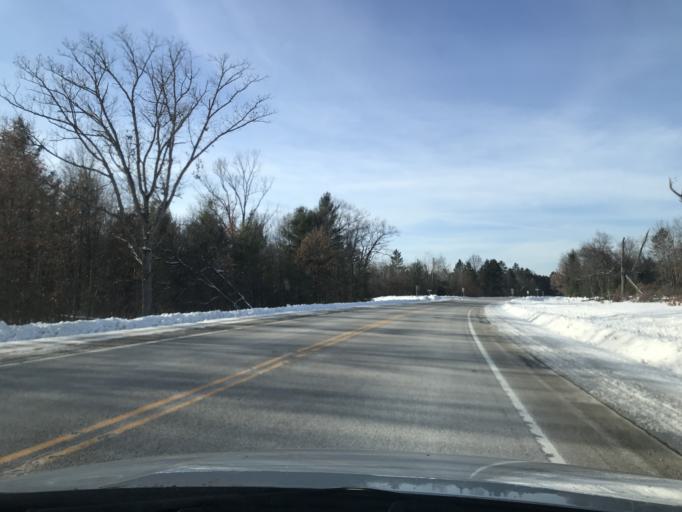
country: US
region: Wisconsin
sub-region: Oconto County
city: Gillett
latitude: 45.1150
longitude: -88.3766
